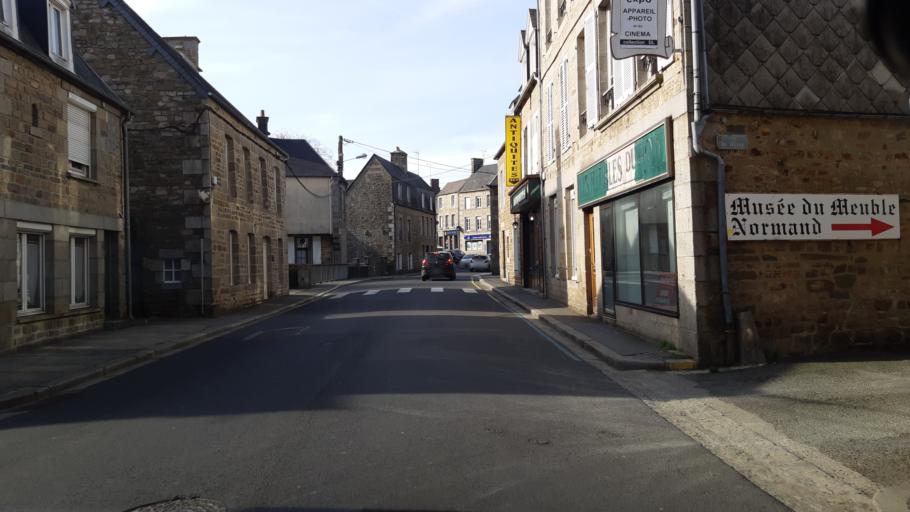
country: FR
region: Lower Normandy
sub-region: Departement de la Manche
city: Villedieu-les-Poeles
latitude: 48.8387
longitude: -1.2239
